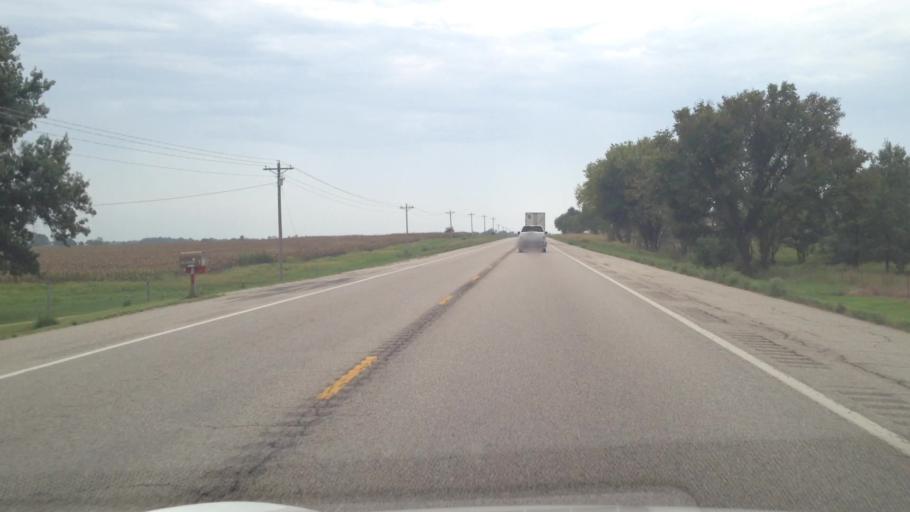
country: US
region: Kansas
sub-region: Crawford County
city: Pittsburg
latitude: 37.2772
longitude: -94.7054
